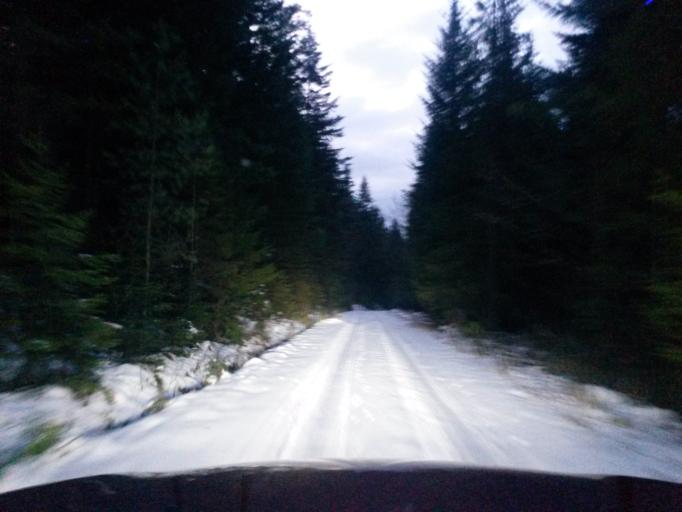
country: SK
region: Kosicky
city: Medzev
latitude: 48.7836
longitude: 20.8137
